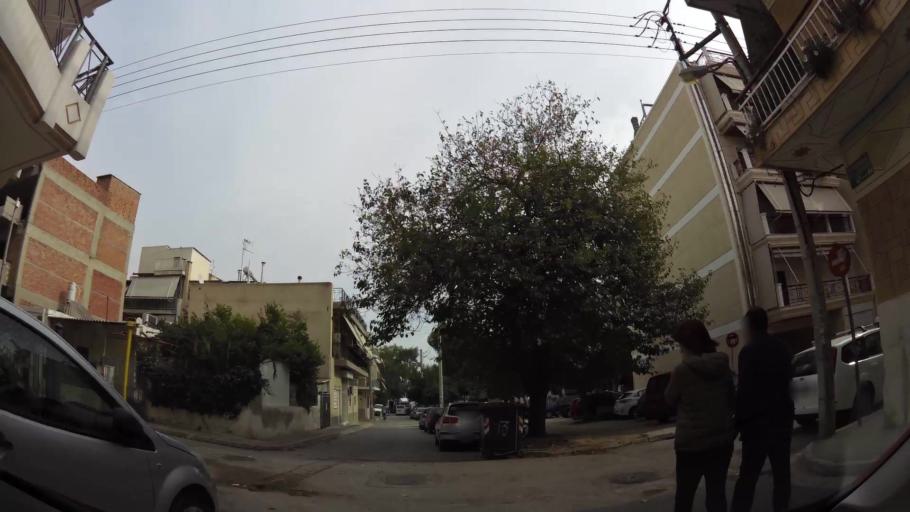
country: GR
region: Attica
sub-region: Nomarchia Athinas
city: Peristeri
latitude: 38.0118
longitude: 23.6806
